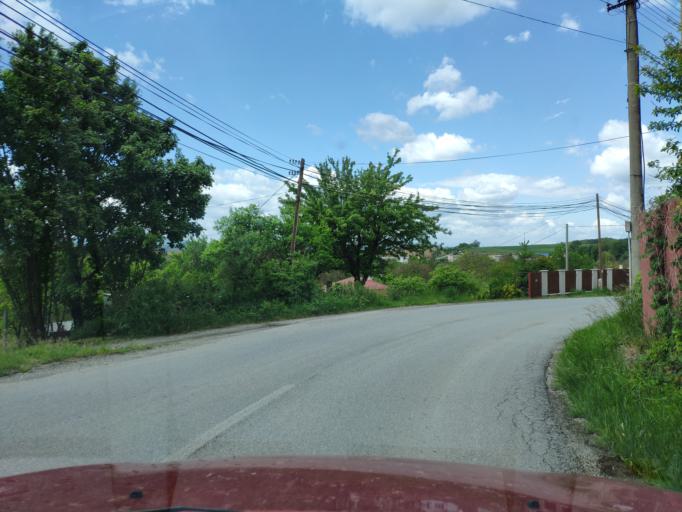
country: SK
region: Kosicky
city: Kosice
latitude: 48.8467
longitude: 21.3205
